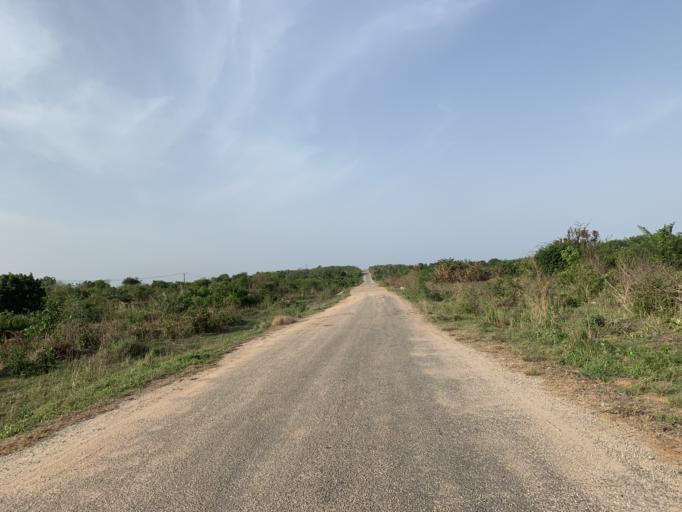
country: GH
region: Central
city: Winneba
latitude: 5.3824
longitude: -0.6076
